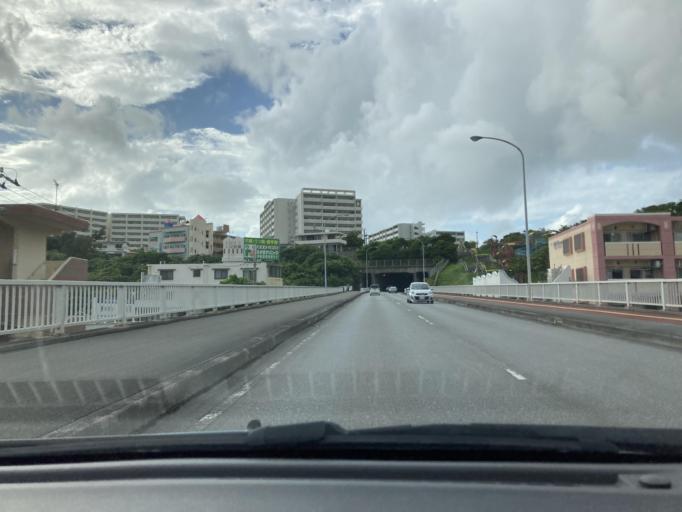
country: JP
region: Okinawa
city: Tomigusuku
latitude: 26.1844
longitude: 127.6752
